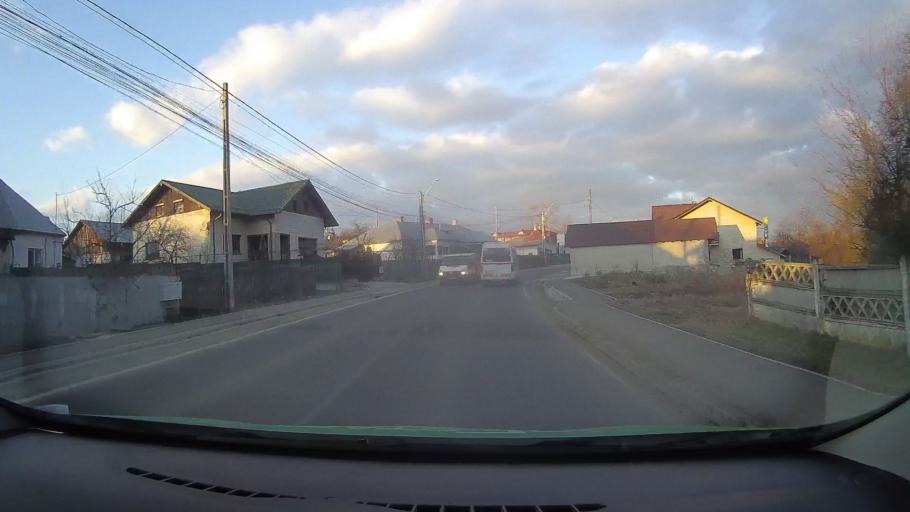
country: RO
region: Dambovita
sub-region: Comuna Gura Ocnitei
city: Gura Ocnitei
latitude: 44.9647
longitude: 25.6002
